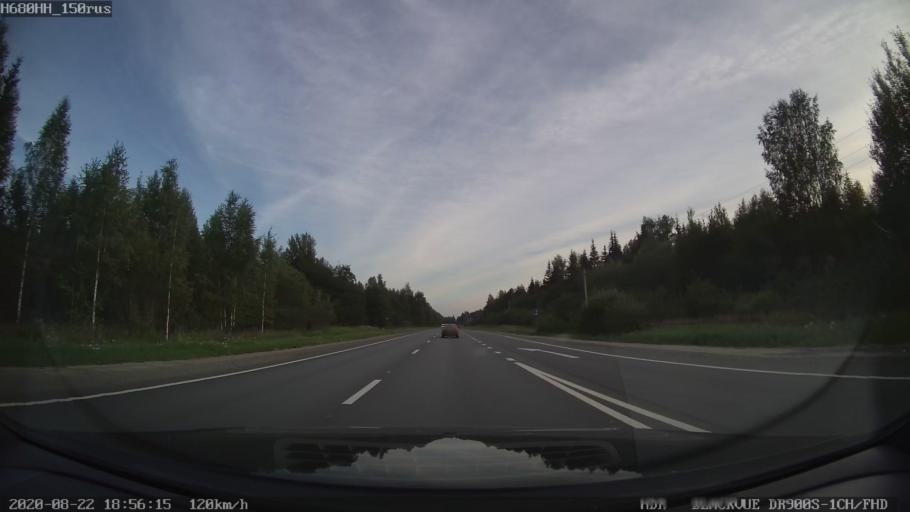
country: RU
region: Tverskaya
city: Rameshki
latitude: 57.1866
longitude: 36.0826
